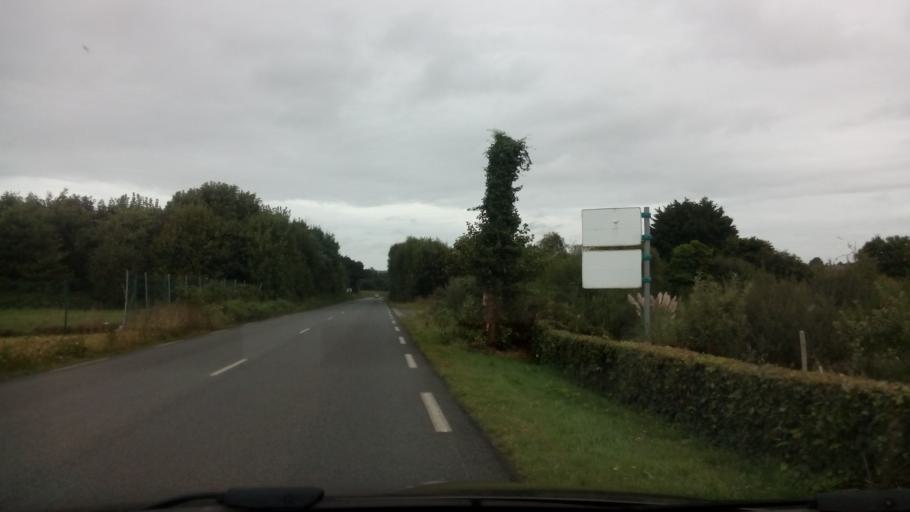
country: FR
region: Brittany
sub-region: Departement du Finistere
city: Morlaix
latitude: 48.5983
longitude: -3.8097
